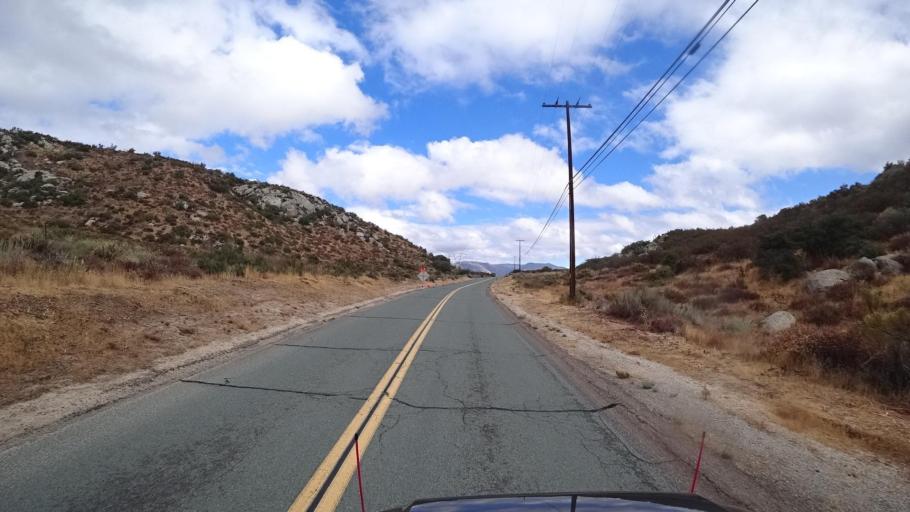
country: US
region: California
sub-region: San Diego County
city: Campo
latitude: 32.7047
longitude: -116.4320
